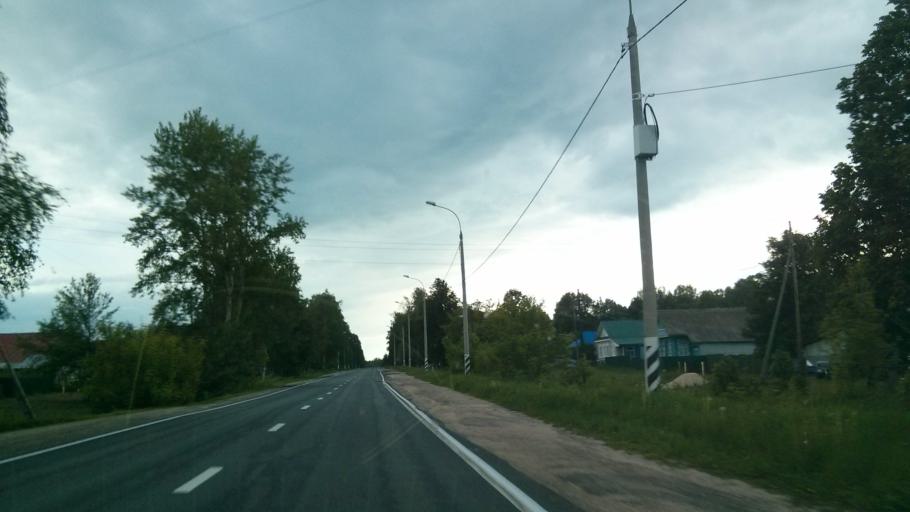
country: RU
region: Nizjnij Novgorod
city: Vacha
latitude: 55.7515
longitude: 42.5108
